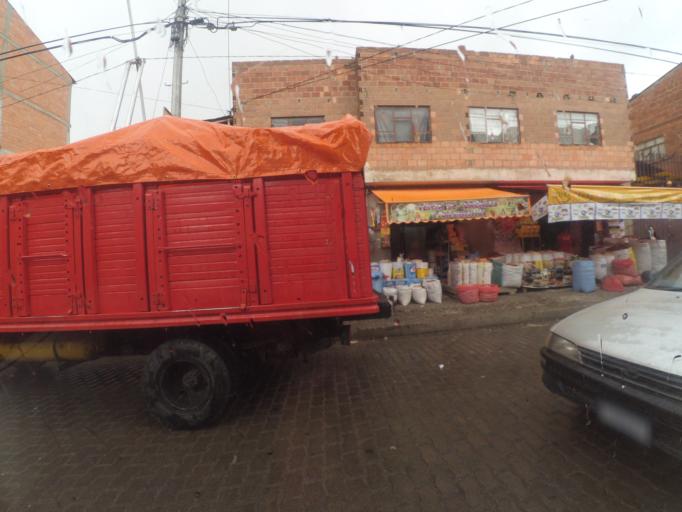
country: BO
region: La Paz
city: La Paz
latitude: -16.5108
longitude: -68.1636
